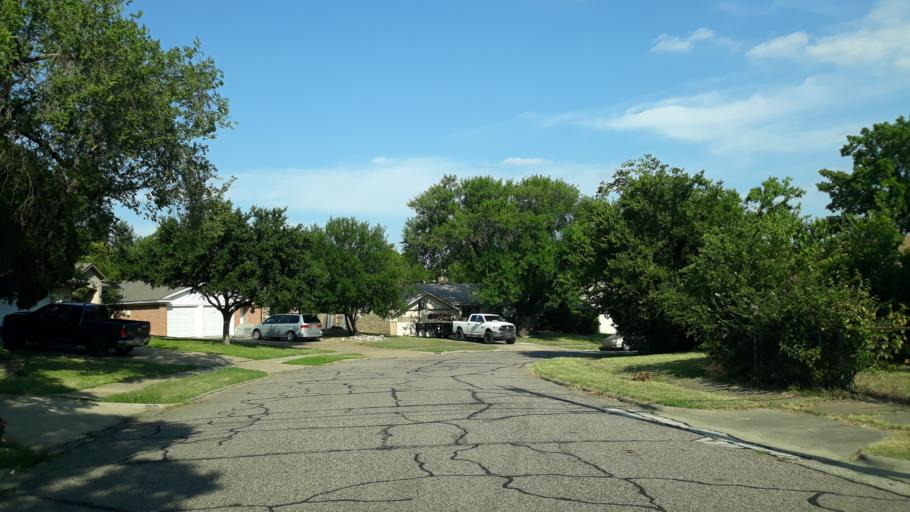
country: US
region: Texas
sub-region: Dallas County
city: Irving
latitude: 32.8435
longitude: -97.0084
